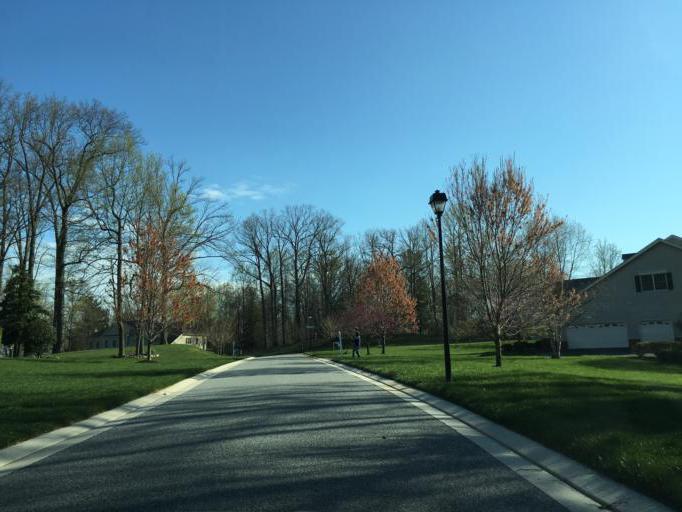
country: US
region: Maryland
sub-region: Baltimore County
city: Hunt Valley
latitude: 39.5074
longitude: -76.6395
